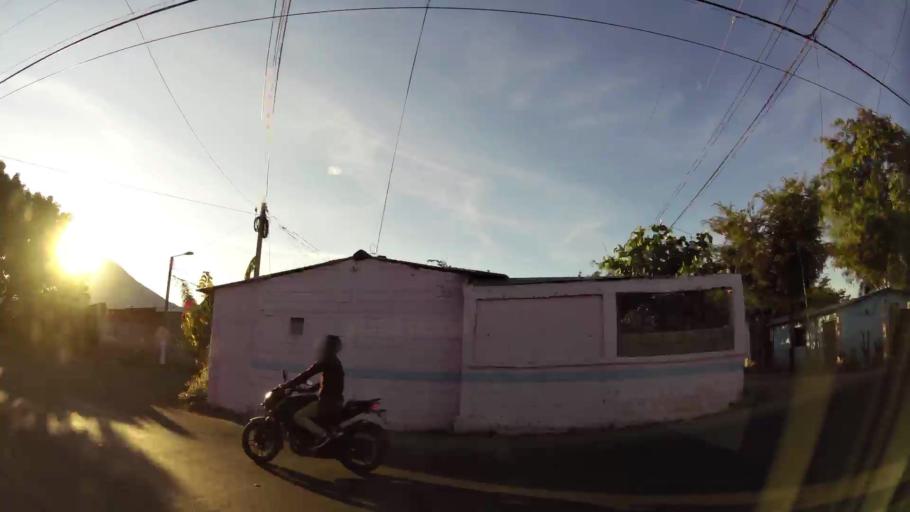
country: SV
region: San Miguel
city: San Miguel
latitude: 13.4711
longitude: -88.1641
